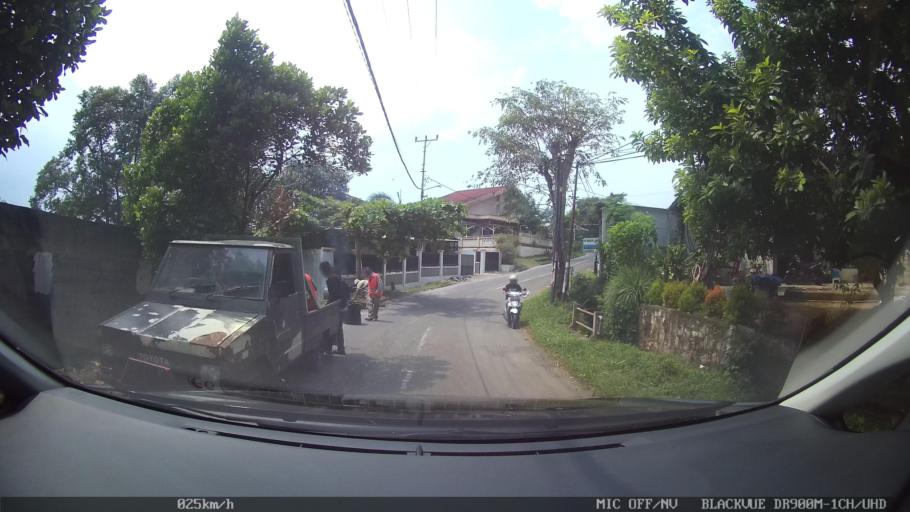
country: ID
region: Lampung
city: Bandarlampung
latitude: -5.4319
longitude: 105.2651
